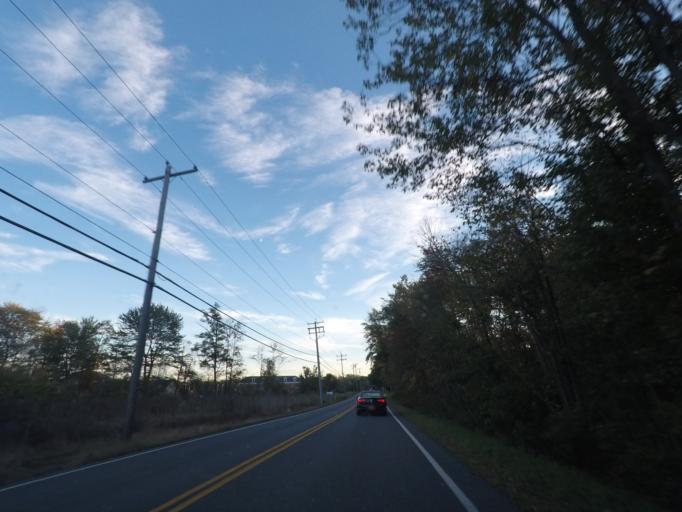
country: US
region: New York
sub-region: Albany County
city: Colonie
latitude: 42.7352
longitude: -73.8265
